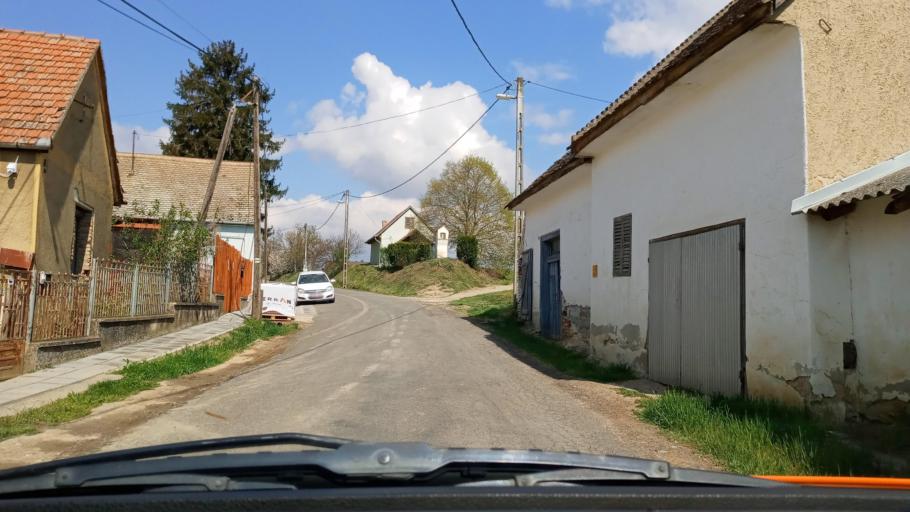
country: HU
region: Baranya
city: Boly
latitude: 46.0804
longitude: 18.5116
